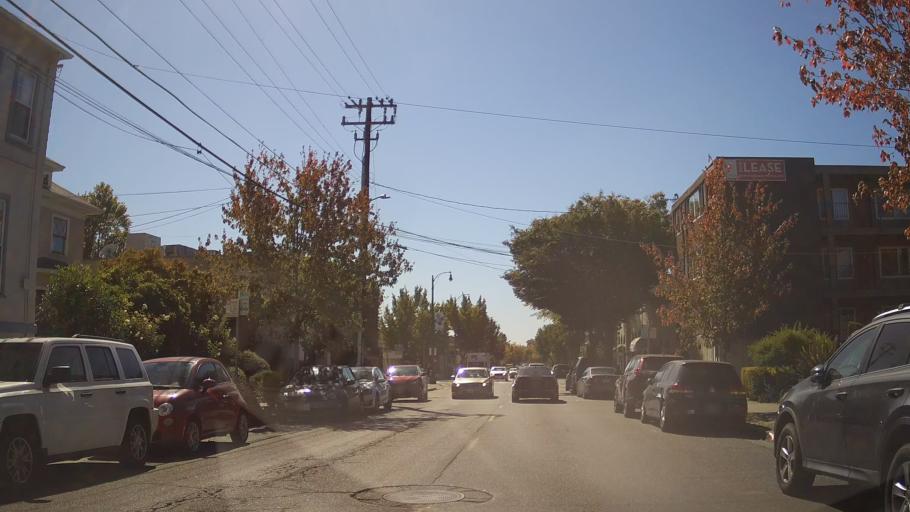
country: US
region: California
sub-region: Alameda County
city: Berkeley
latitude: 37.8592
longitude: -122.2533
